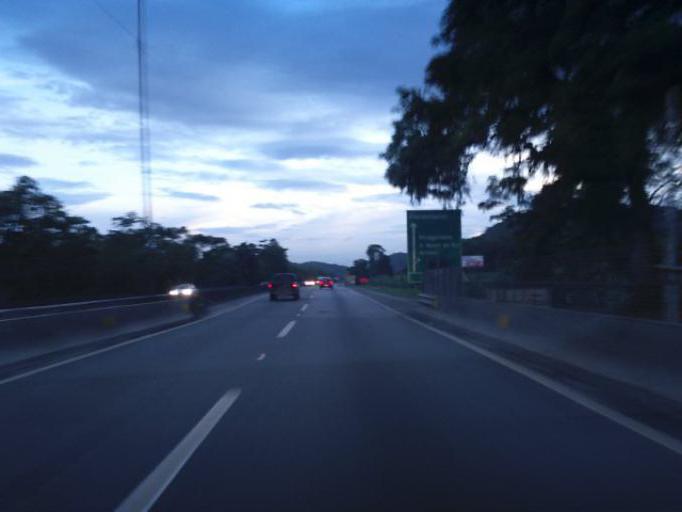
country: BR
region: Santa Catarina
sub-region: Joinville
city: Joinville
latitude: -26.1959
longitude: -48.9124
